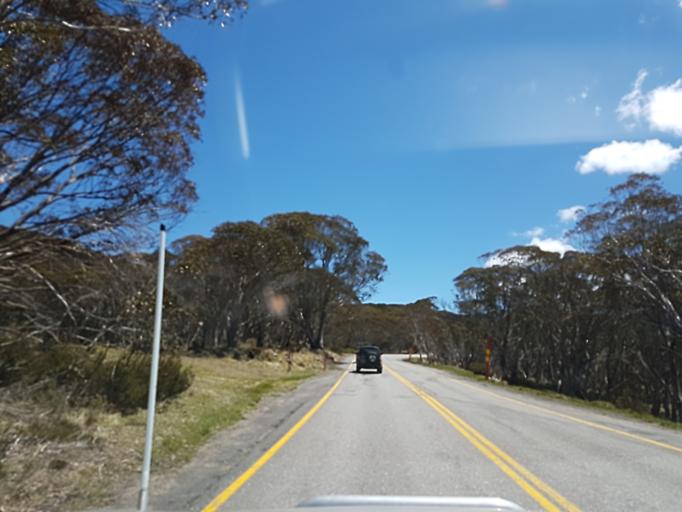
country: AU
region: Victoria
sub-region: Alpine
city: Mount Beauty
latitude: -37.0134
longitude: 147.1912
